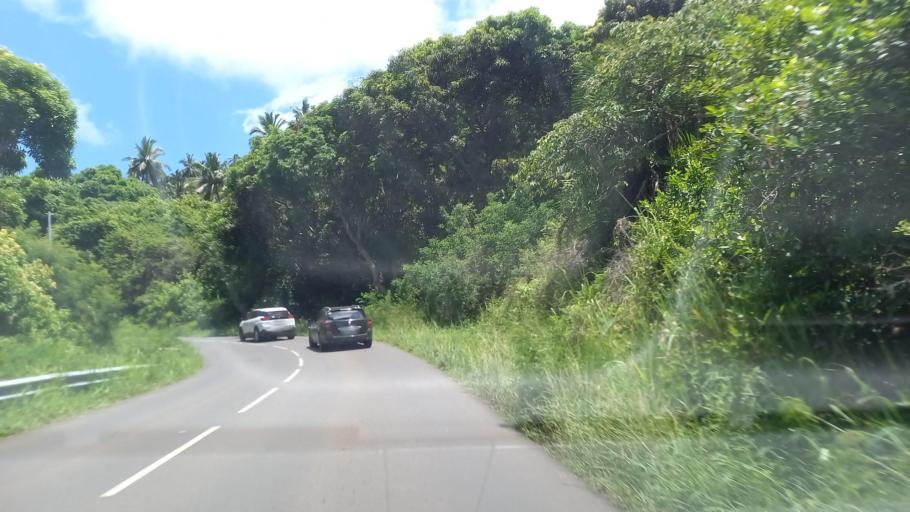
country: YT
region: Sada
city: Sada
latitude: -12.8603
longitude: 45.1052
